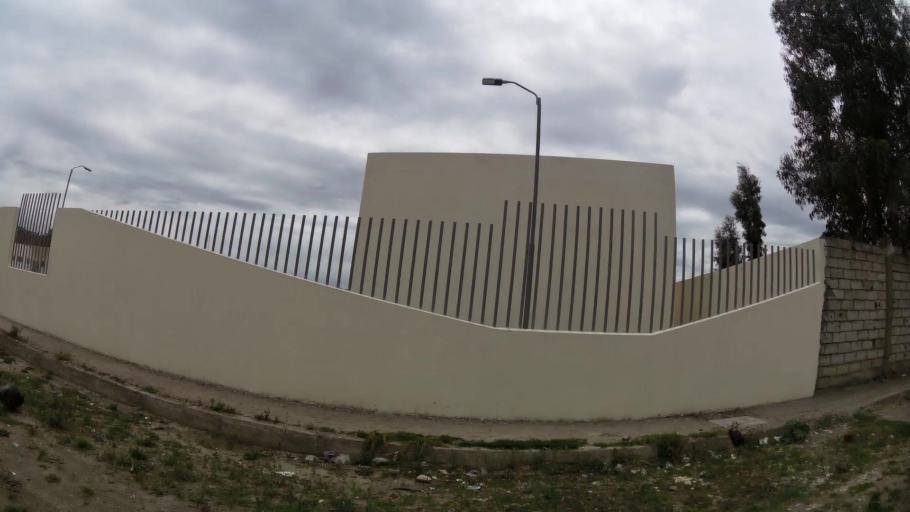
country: EC
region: Cotopaxi
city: Latacunga
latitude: -0.9507
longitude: -78.6036
